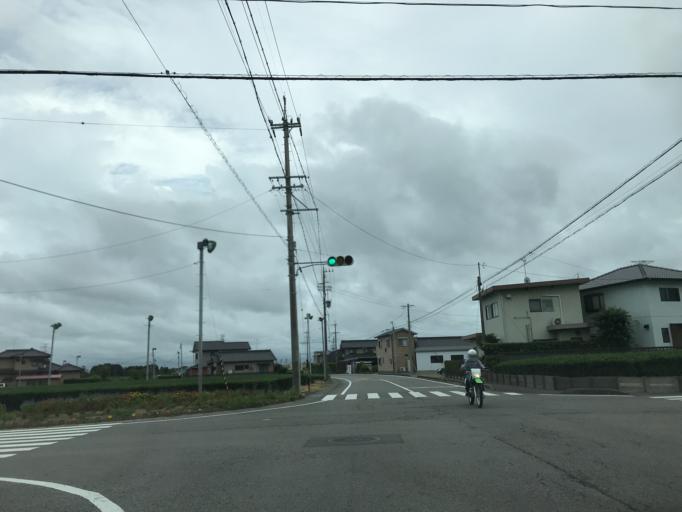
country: JP
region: Shizuoka
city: Sagara
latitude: 34.7037
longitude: 138.1451
